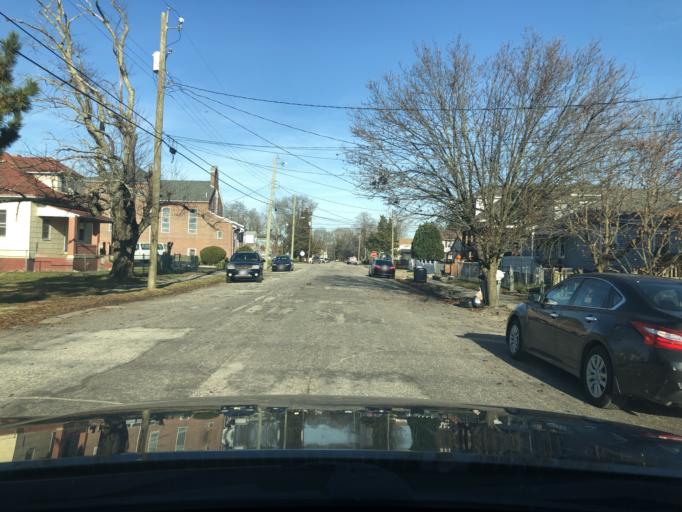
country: US
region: New Jersey
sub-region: Atlantic County
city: Northfield
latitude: 39.3838
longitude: -74.5404
